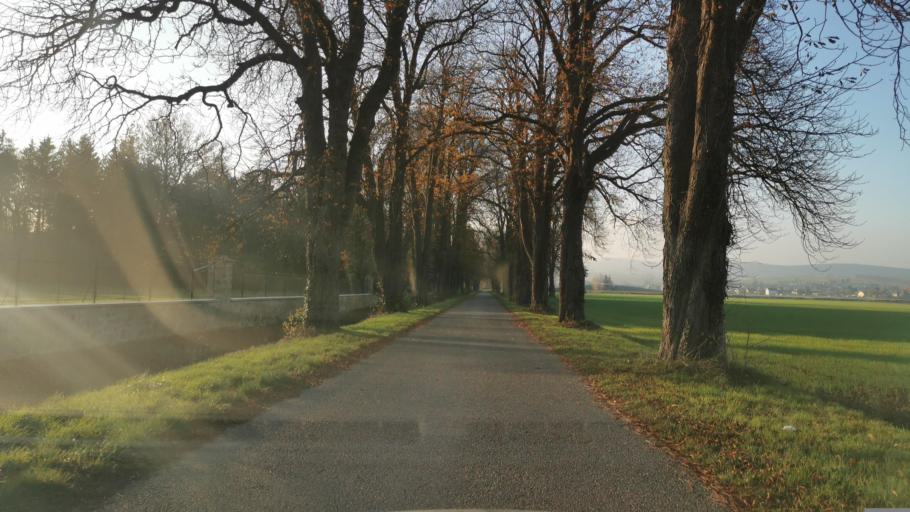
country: AT
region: Lower Austria
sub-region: Politischer Bezirk Korneuburg
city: Stetten
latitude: 48.3819
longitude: 16.3878
